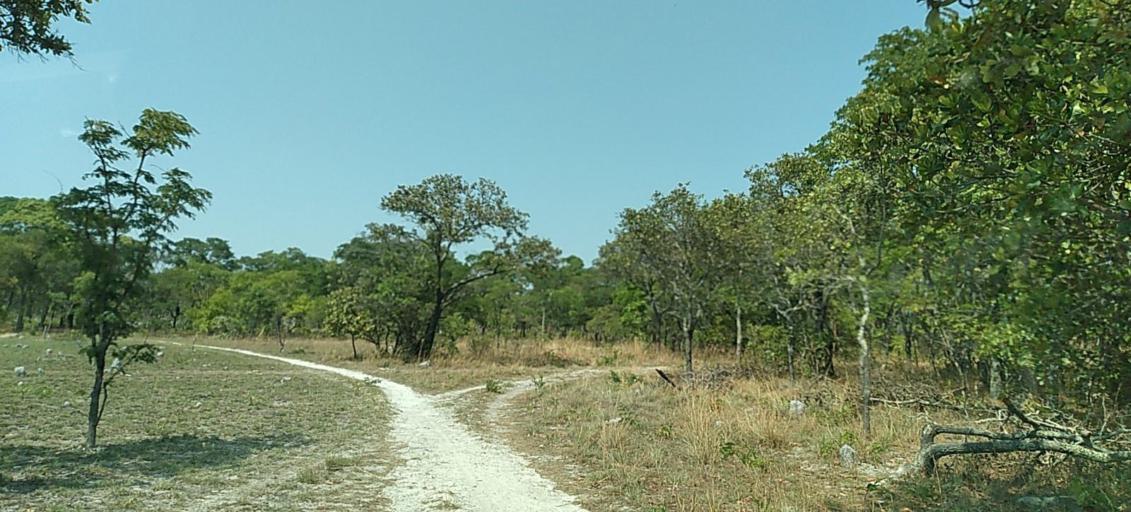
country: ZM
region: Copperbelt
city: Mpongwe
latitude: -13.7855
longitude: 28.1025
